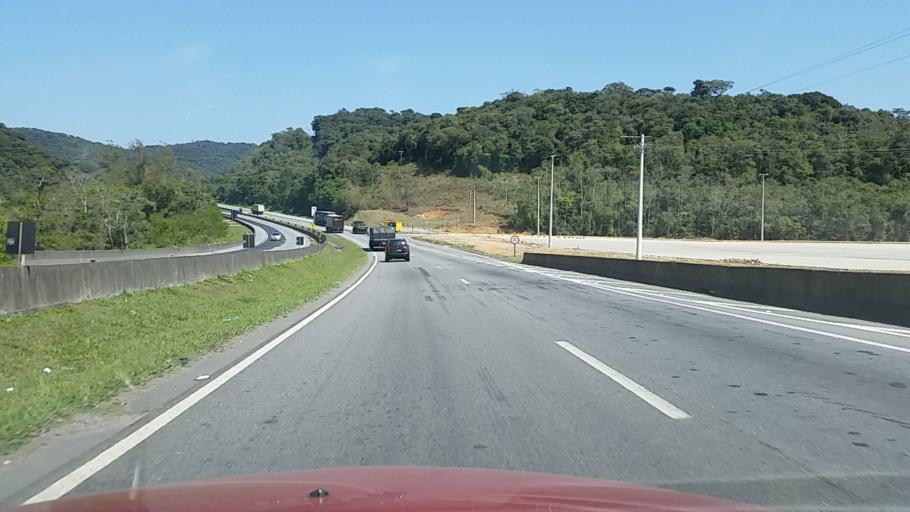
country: BR
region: Sao Paulo
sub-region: Juquitiba
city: Juquitiba
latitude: -24.0202
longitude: -47.1715
